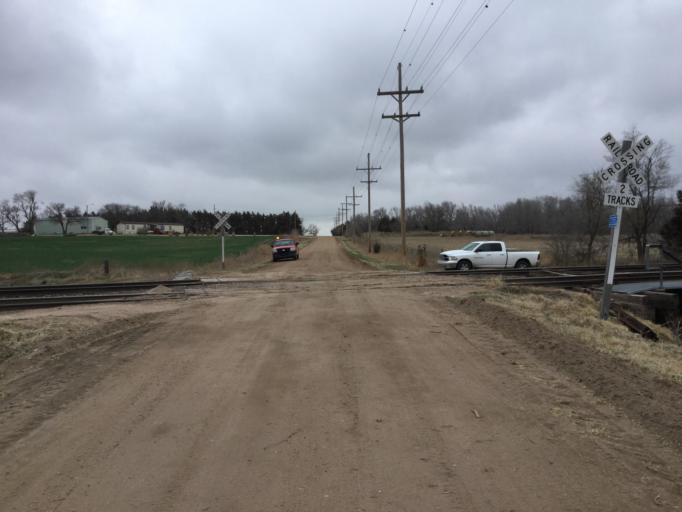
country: US
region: Kansas
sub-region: Barton County
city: Hoisington
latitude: 38.5169
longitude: -98.7567
